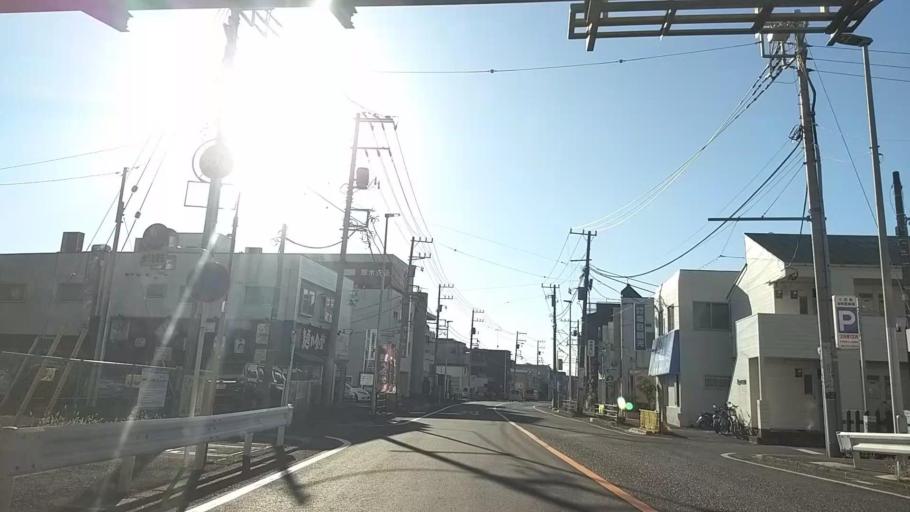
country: JP
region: Kanagawa
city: Atsugi
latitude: 35.4415
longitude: 139.3704
